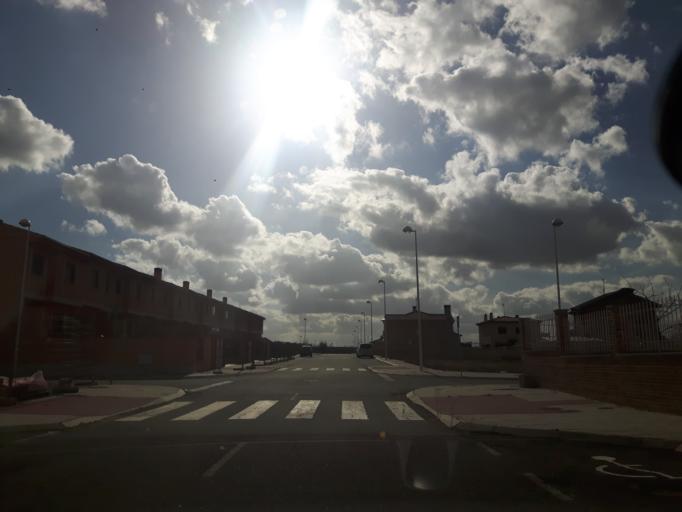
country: ES
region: Castille and Leon
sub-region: Provincia de Salamanca
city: Moriscos
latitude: 41.0081
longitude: -5.5882
